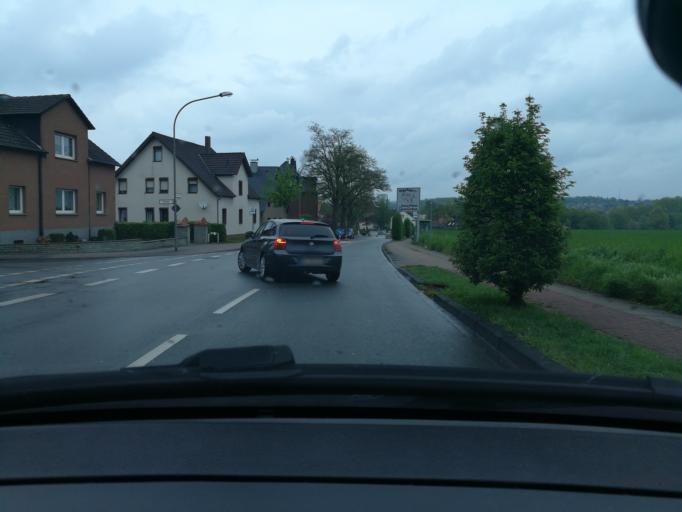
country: DE
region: North Rhine-Westphalia
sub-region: Regierungsbezirk Detmold
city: Herford
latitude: 52.0999
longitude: 8.6821
